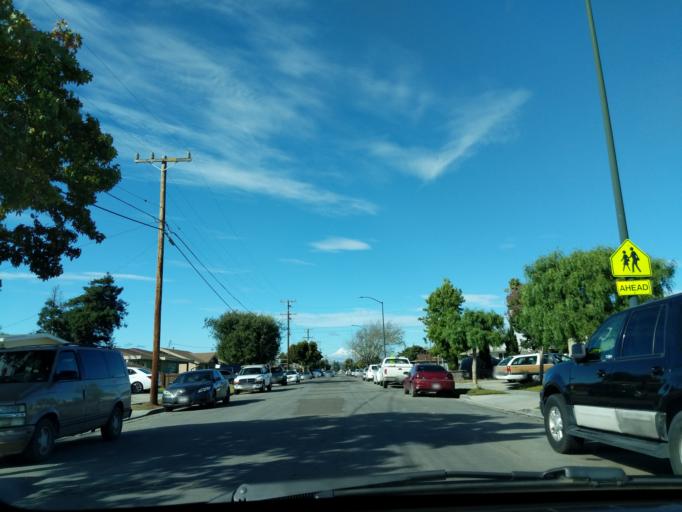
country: US
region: California
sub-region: Monterey County
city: Salinas
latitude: 36.6706
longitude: -121.6327
